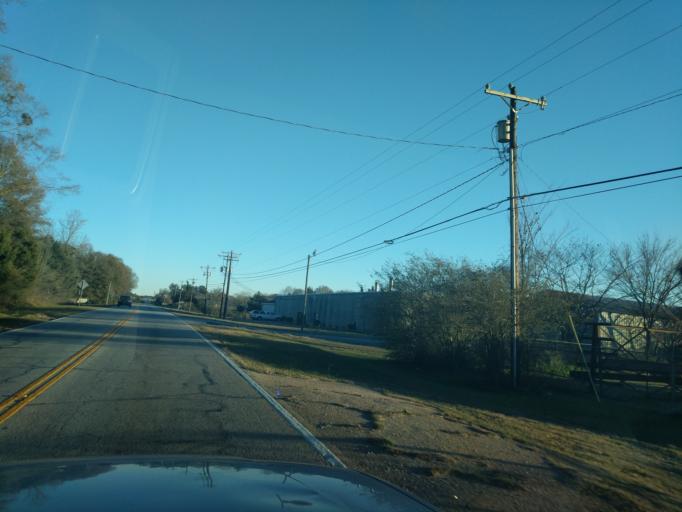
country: US
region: Georgia
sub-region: Hart County
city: Reed Creek
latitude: 34.5454
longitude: -82.8620
